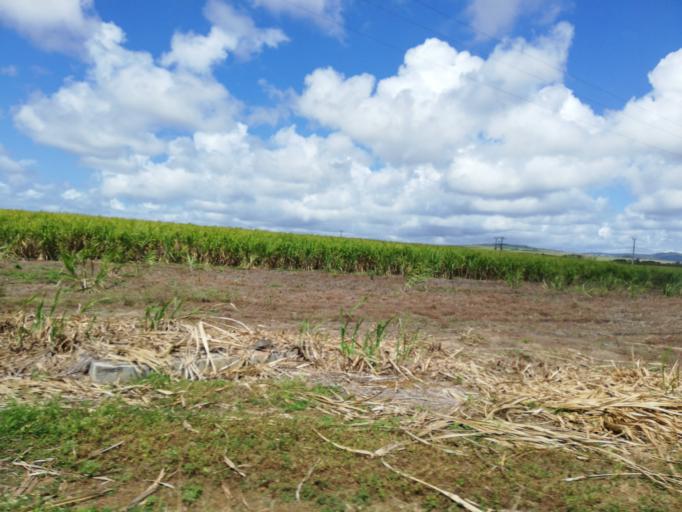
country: MU
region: Riviere du Rempart
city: Cottage
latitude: -20.0700
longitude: 57.6232
